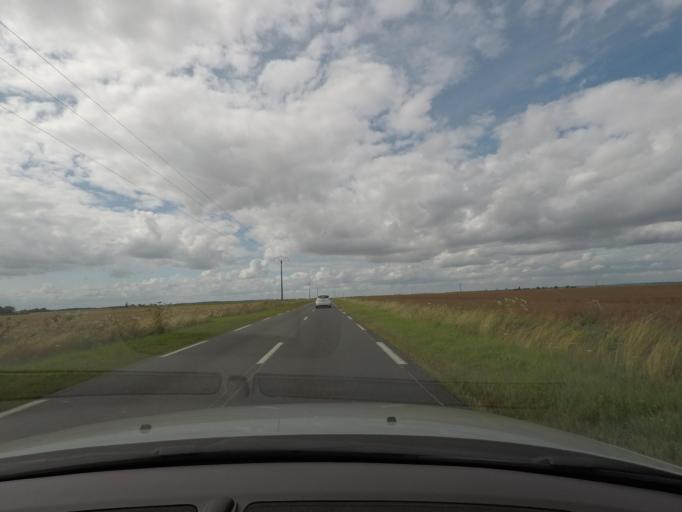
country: FR
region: Haute-Normandie
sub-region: Departement de l'Eure
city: Les Andelys
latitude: 49.2033
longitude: 1.4692
